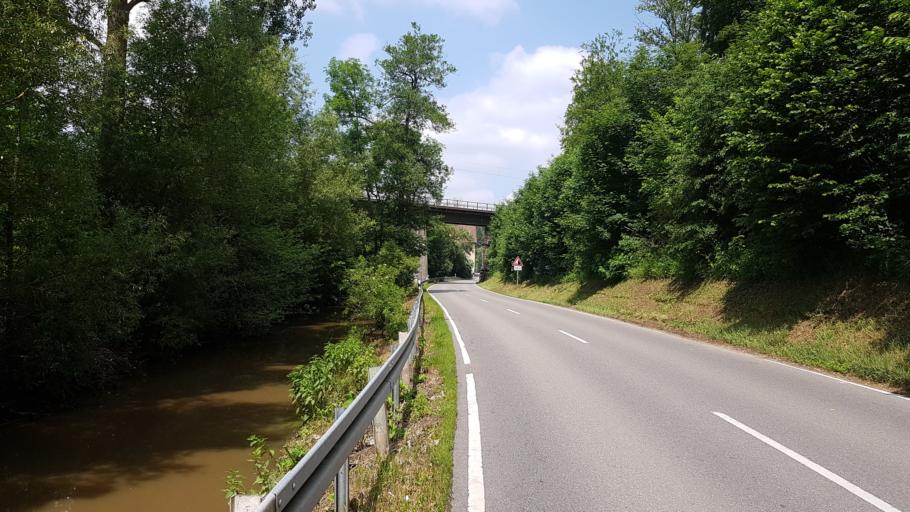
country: DE
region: Baden-Wuerttemberg
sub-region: Regierungsbezirk Stuttgart
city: Weil der Stadt
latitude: 48.7604
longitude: 8.8809
